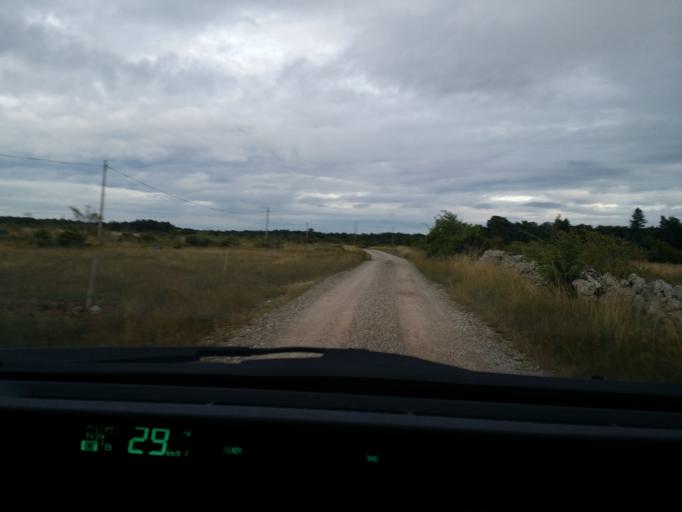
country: SE
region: Kalmar
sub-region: Borgholms Kommun
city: Borgholm
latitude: 57.2131
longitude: 16.9492
